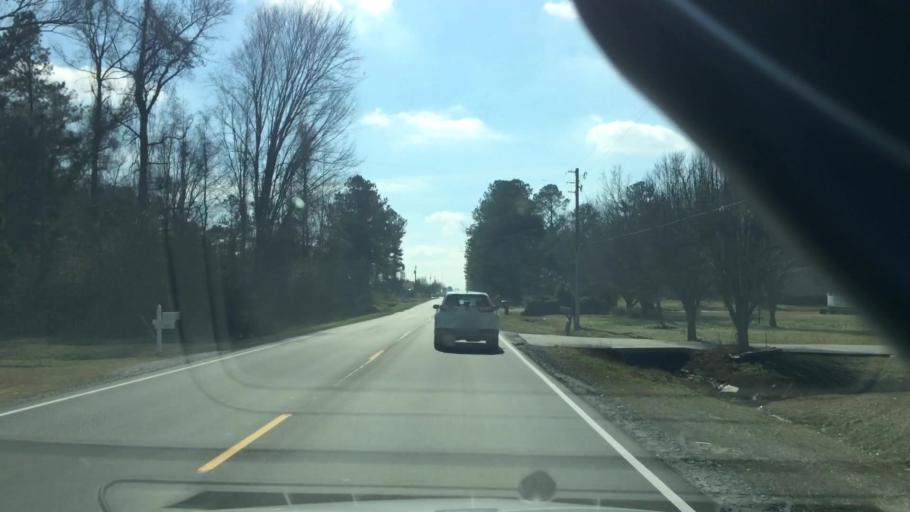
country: US
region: North Carolina
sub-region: Duplin County
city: Beulaville
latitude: 34.9343
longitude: -77.7710
